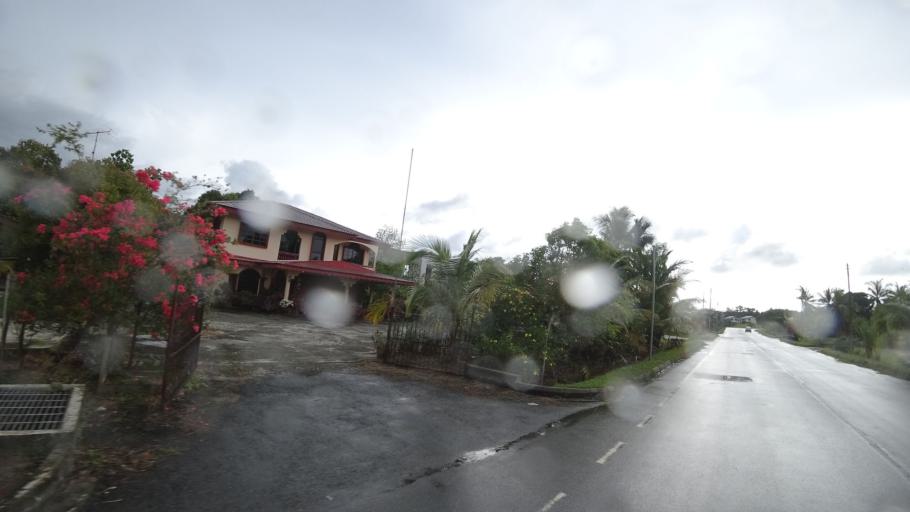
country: BN
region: Brunei and Muara
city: Bandar Seri Begawan
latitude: 4.8353
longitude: 114.9145
